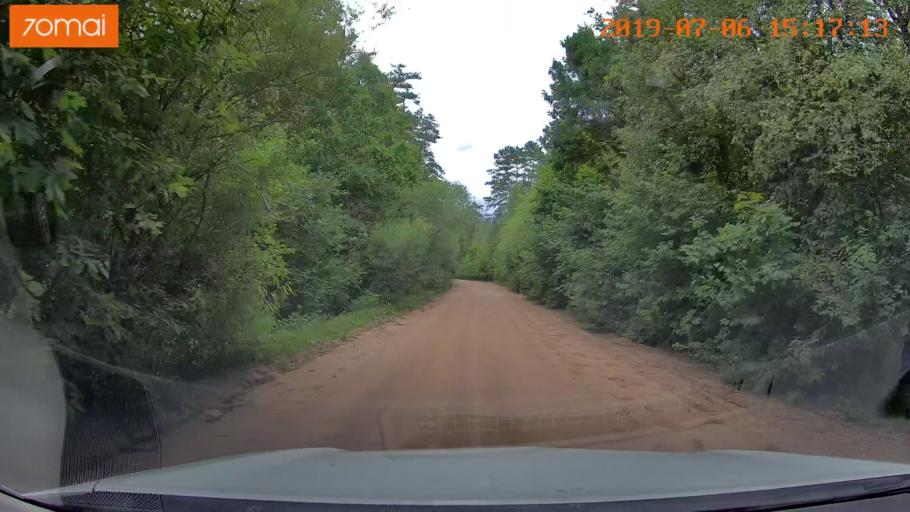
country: BY
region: Minsk
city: Ivyanyets
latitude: 53.9867
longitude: 26.6685
